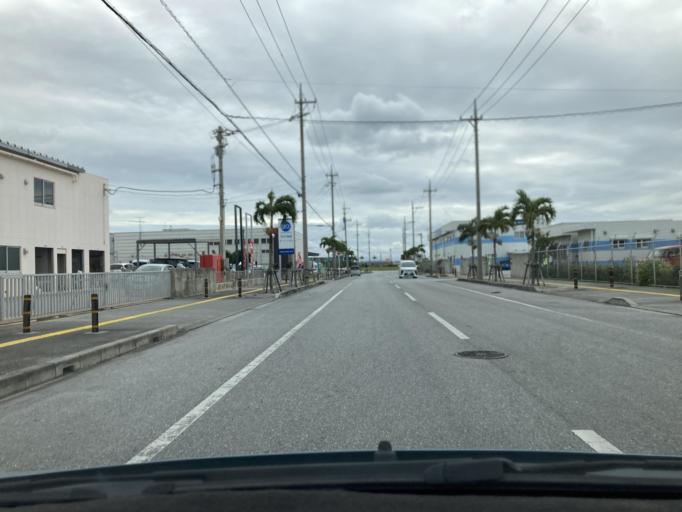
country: JP
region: Okinawa
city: Itoman
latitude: 26.1545
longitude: 127.6534
